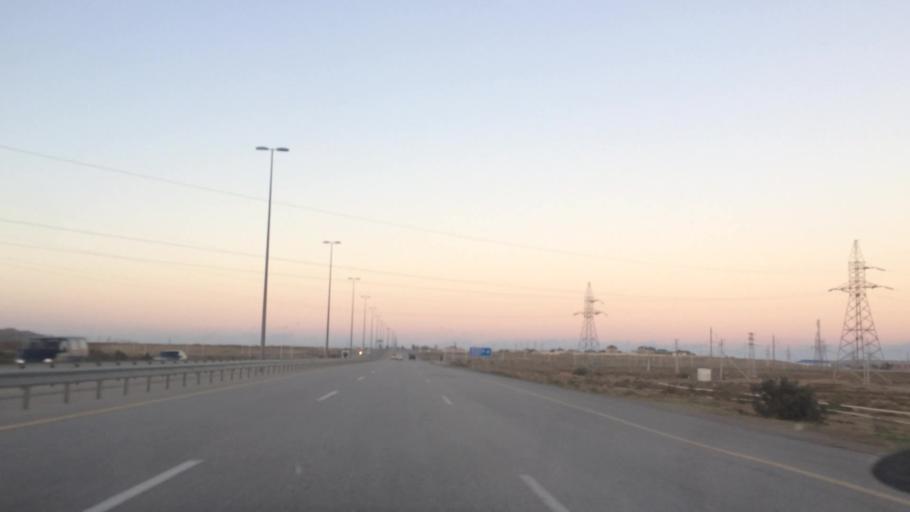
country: AZ
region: Baki
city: Qobustan
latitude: 39.9771
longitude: 49.4201
